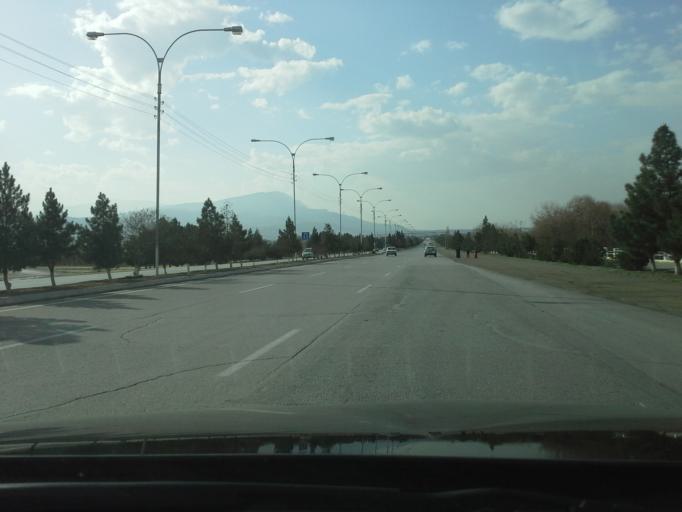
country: TM
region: Ahal
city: Abadan
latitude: 37.9716
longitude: 58.2612
